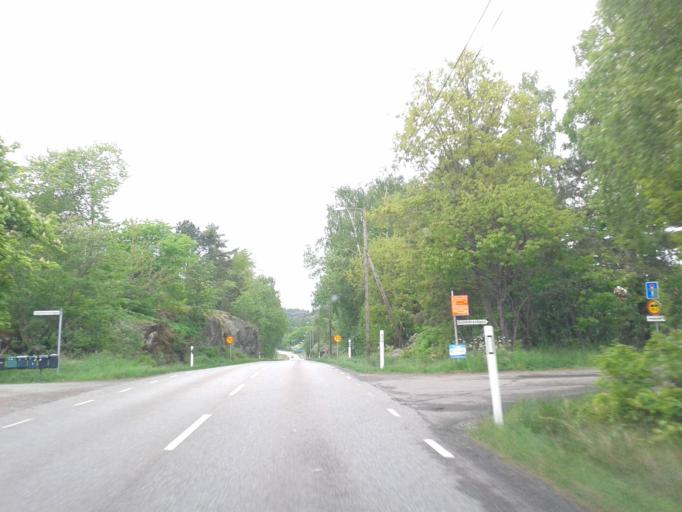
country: SE
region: Vaestra Goetaland
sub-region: Kungalvs Kommun
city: Kode
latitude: 57.8957
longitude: 11.7375
